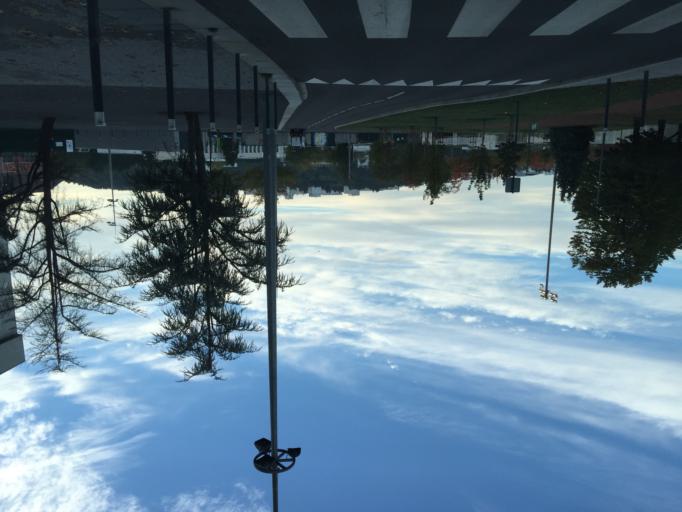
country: FR
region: Rhone-Alpes
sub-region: Departement de la Loire
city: Saint-Priest-en-Jarez
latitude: 45.4614
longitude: 4.3887
